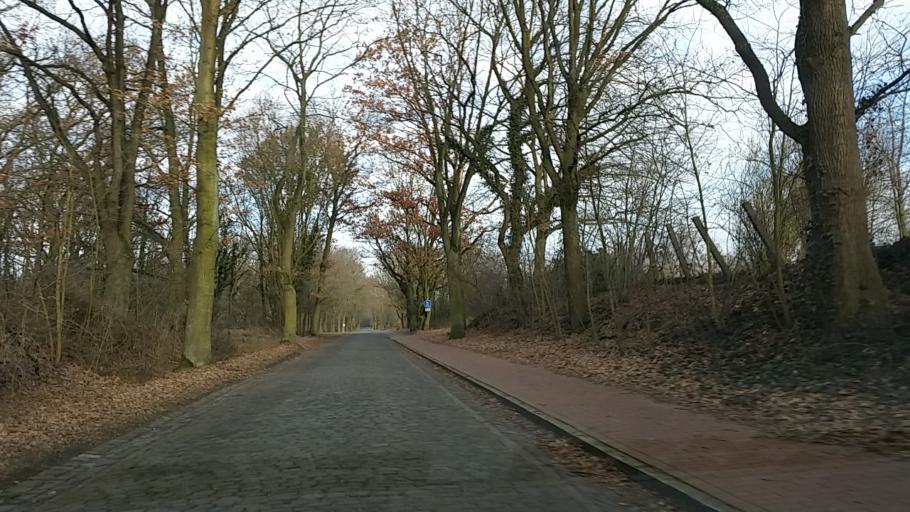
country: DE
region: Lower Saxony
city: Brome
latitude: 52.6042
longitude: 10.9354
